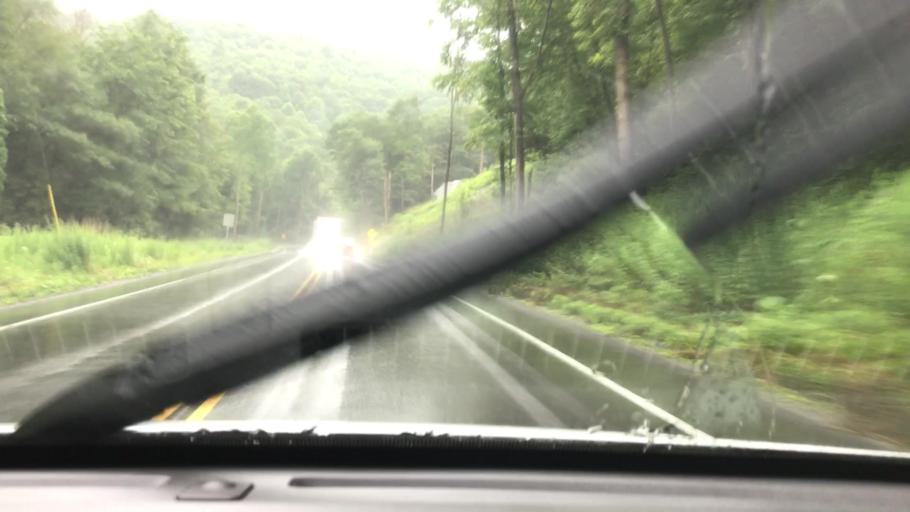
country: US
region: Pennsylvania
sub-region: Blair County
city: Tyrone
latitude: 40.7616
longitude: -78.2318
